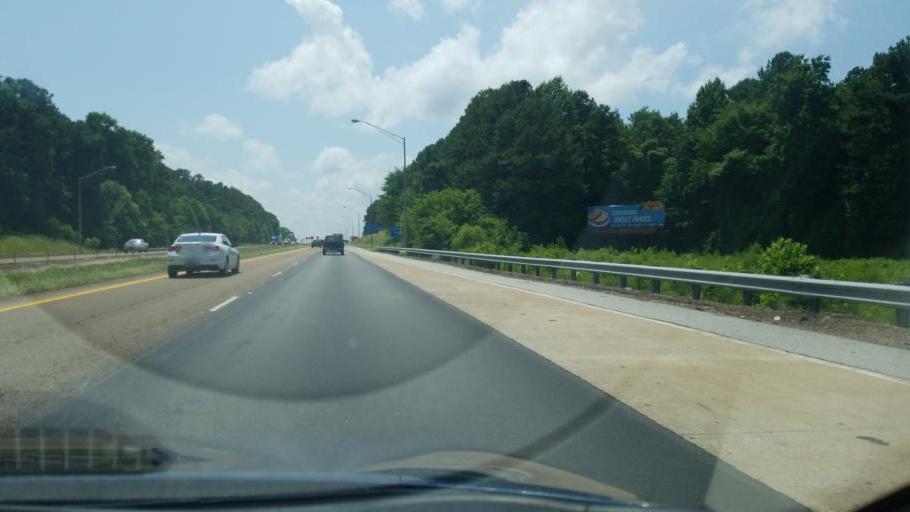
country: US
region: Tennessee
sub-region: Madison County
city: Jackson
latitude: 35.6733
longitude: -88.8154
